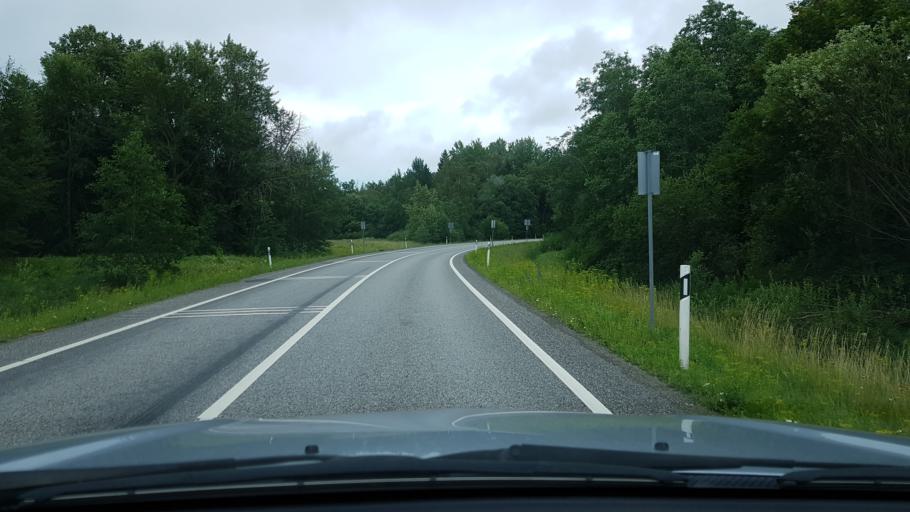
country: EE
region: Ida-Virumaa
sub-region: Narva-Joesuu linn
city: Narva-Joesuu
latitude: 59.3635
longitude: 27.9327
